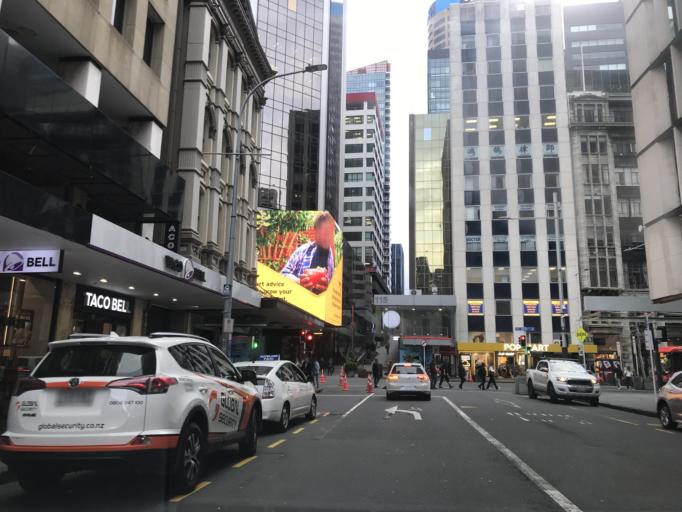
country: NZ
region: Auckland
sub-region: Auckland
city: Auckland
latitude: -36.8466
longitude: 174.7666
